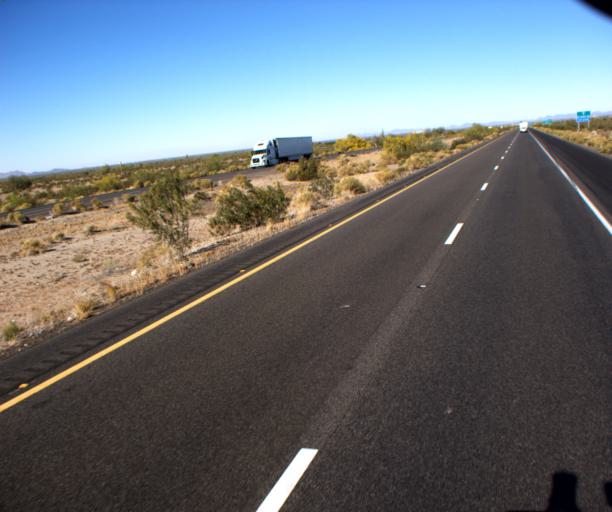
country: US
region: Arizona
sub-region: Maricopa County
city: Gila Bend
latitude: 32.9175
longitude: -112.6350
